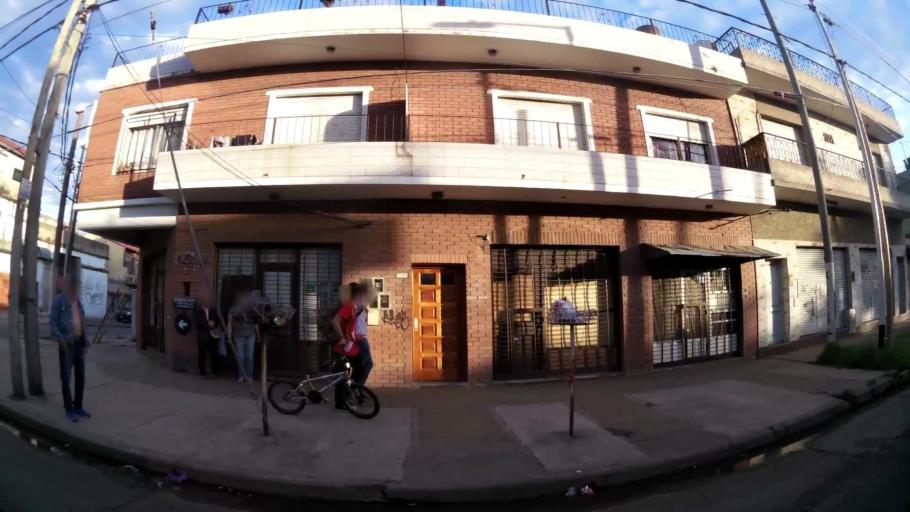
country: AR
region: Buenos Aires
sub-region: Partido de Avellaneda
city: Avellaneda
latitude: -34.7078
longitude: -58.3392
